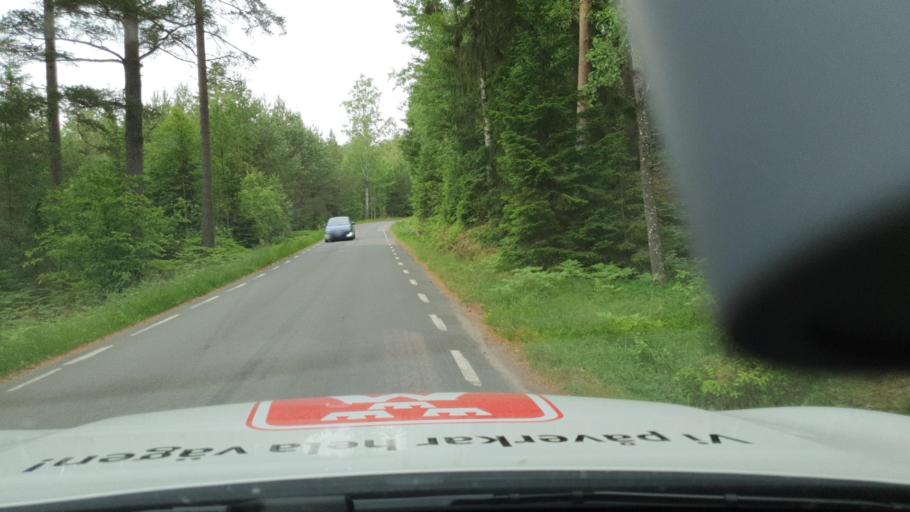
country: SE
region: Vaestra Goetaland
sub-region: Tidaholms Kommun
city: Olofstorp
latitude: 58.1927
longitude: 14.0947
